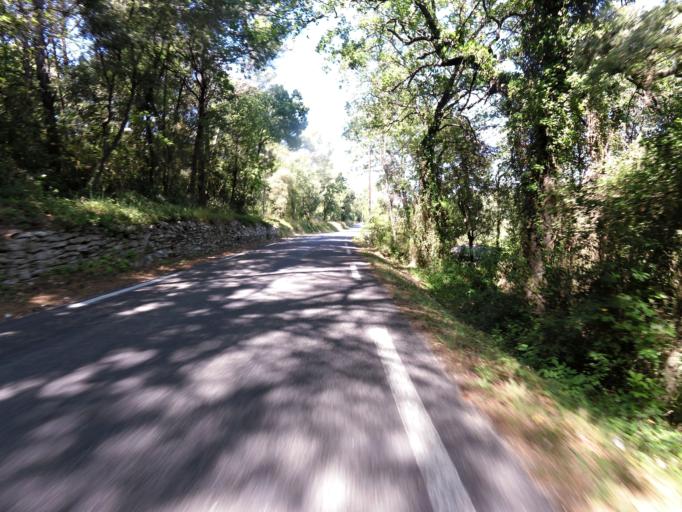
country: FR
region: Languedoc-Roussillon
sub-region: Departement du Gard
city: Sommieres
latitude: 43.8129
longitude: 4.0675
